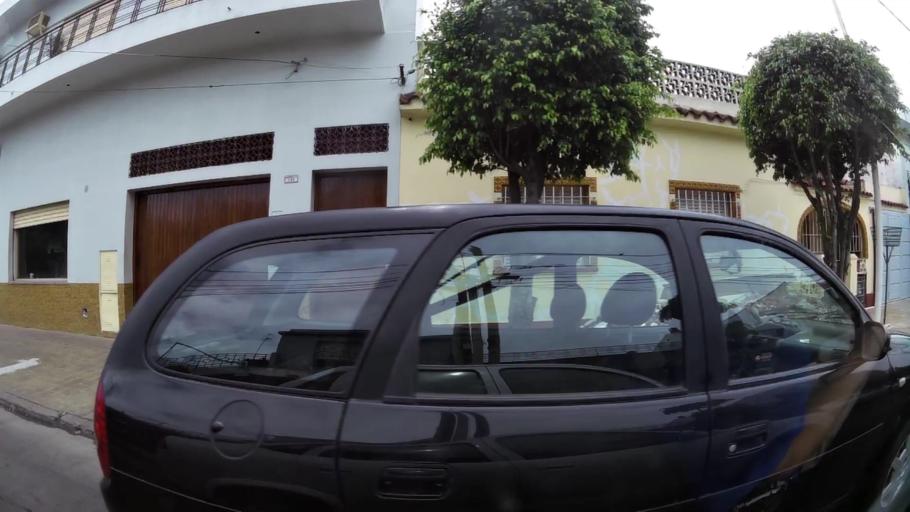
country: AR
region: Buenos Aires
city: San Justo
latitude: -34.6743
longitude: -58.5398
